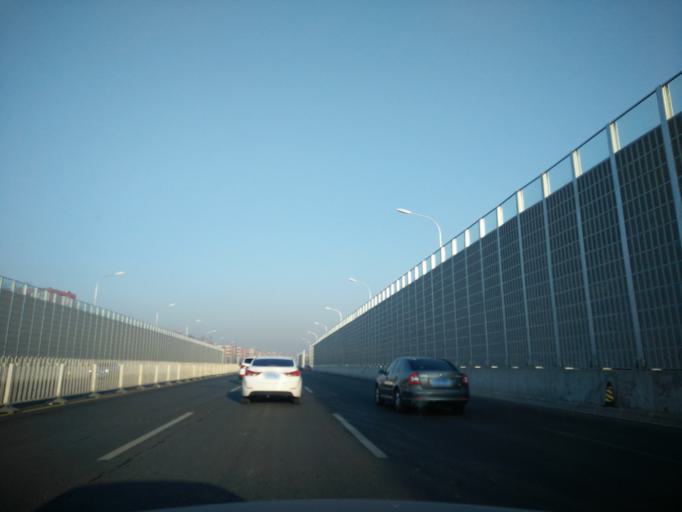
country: CN
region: Beijing
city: Jiugong
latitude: 39.7902
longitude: 116.4807
